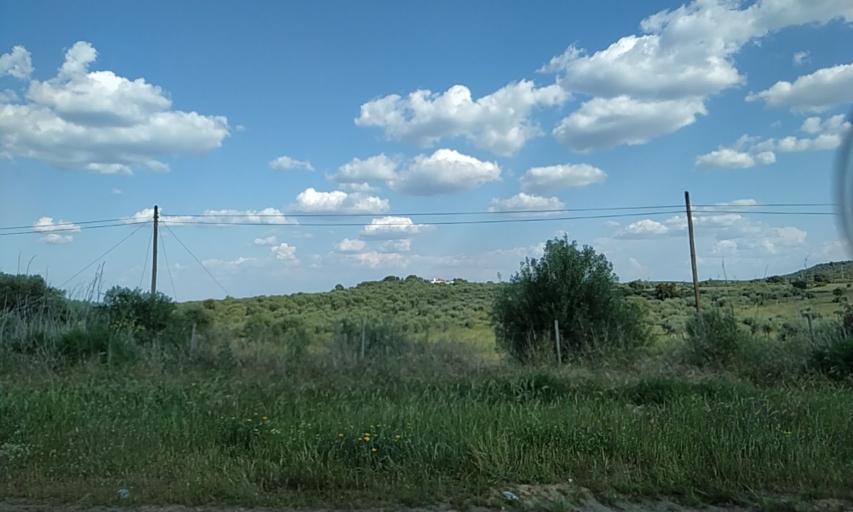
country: PT
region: Evora
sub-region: Estremoz
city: Estremoz
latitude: 38.8614
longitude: -7.5736
